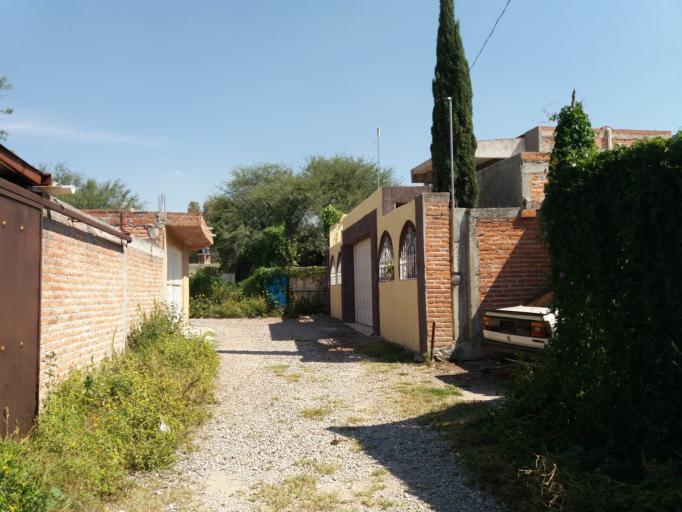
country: MX
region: Aguascalientes
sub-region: Aguascalientes
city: Penuelas (El Cienegal)
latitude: 21.7570
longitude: -102.3041
